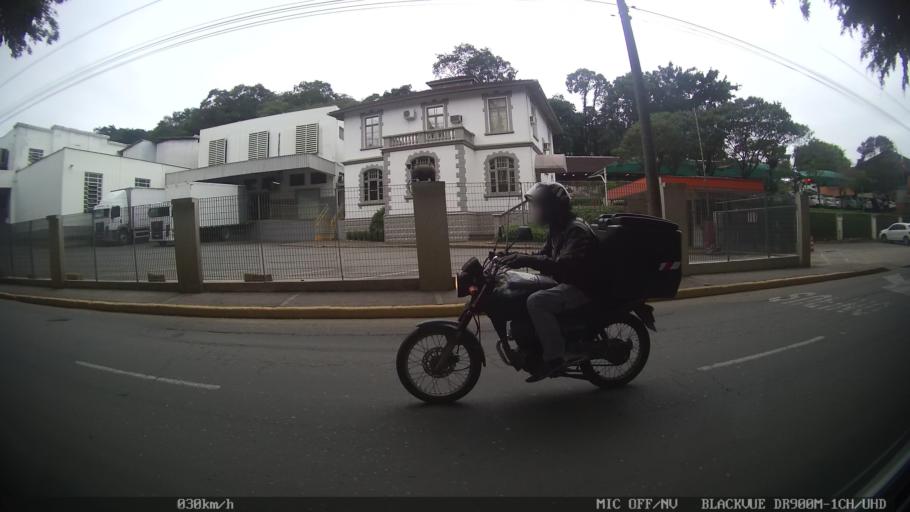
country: BR
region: Santa Catarina
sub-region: Joinville
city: Joinville
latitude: -26.2991
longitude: -48.8419
